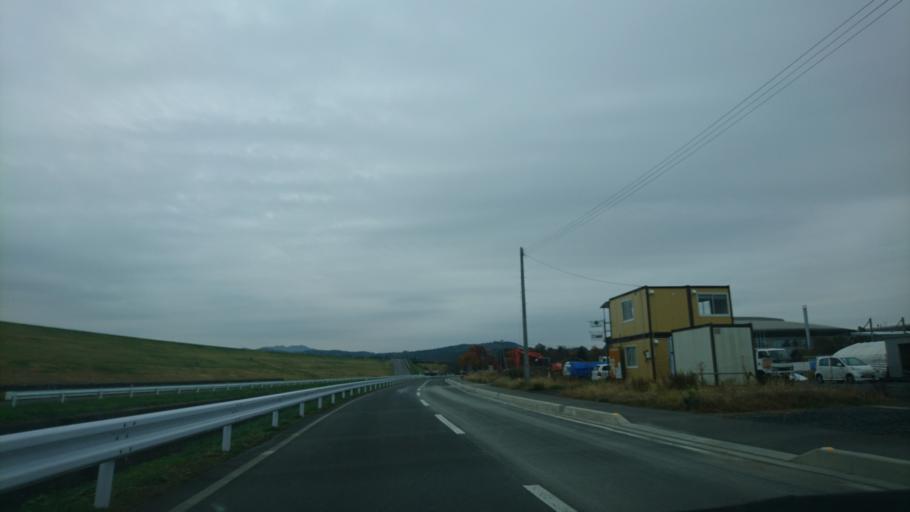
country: JP
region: Iwate
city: Ichinoseki
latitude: 38.9426
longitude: 141.1533
